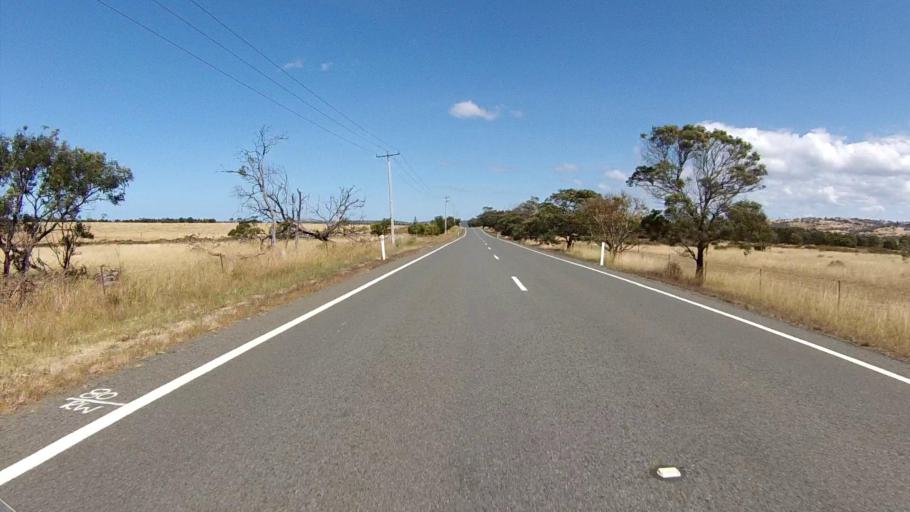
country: AU
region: Tasmania
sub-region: Break O'Day
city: St Helens
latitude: -42.0921
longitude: 148.0656
